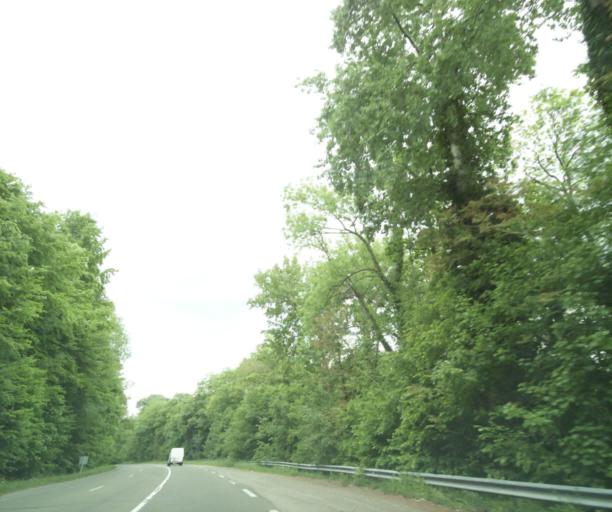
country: FR
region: Ile-de-France
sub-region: Departement des Yvelines
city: Flins-sur-Seine
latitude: 48.9609
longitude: 1.8669
